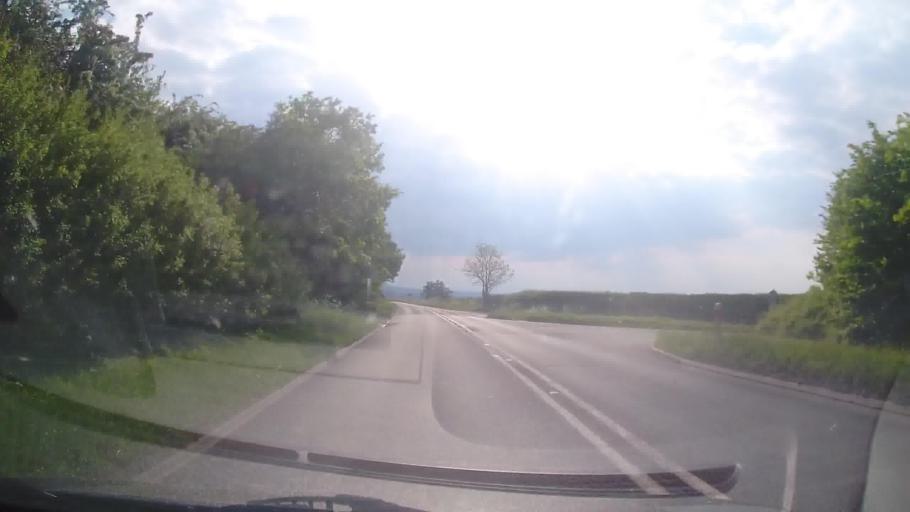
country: GB
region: England
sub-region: Shropshire
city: Withington
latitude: 52.6940
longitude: -2.5776
